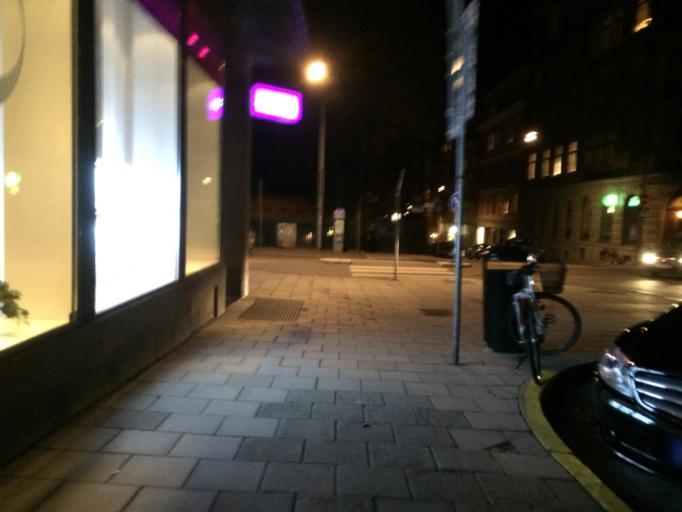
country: SE
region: Stockholm
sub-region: Stockholms Kommun
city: OEstermalm
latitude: 59.3345
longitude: 18.0866
